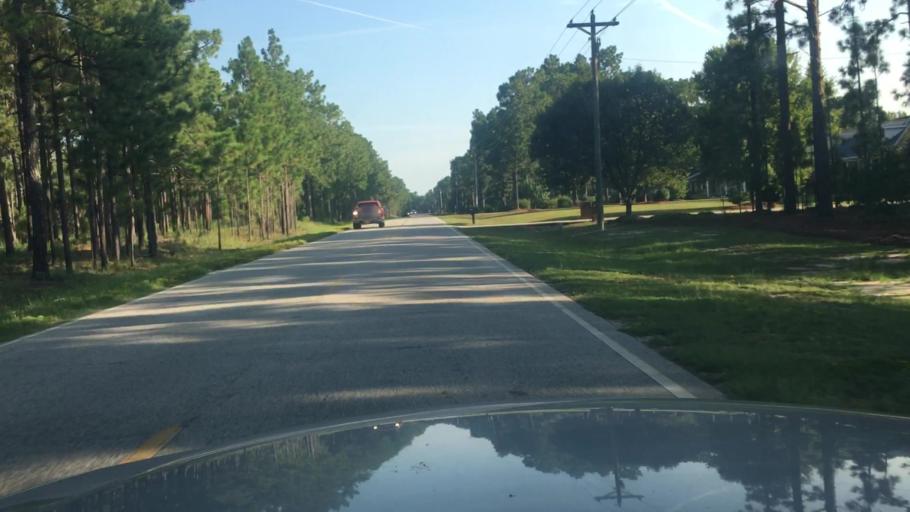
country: US
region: North Carolina
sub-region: Harnett County
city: Walkertown
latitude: 35.2171
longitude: -78.8652
